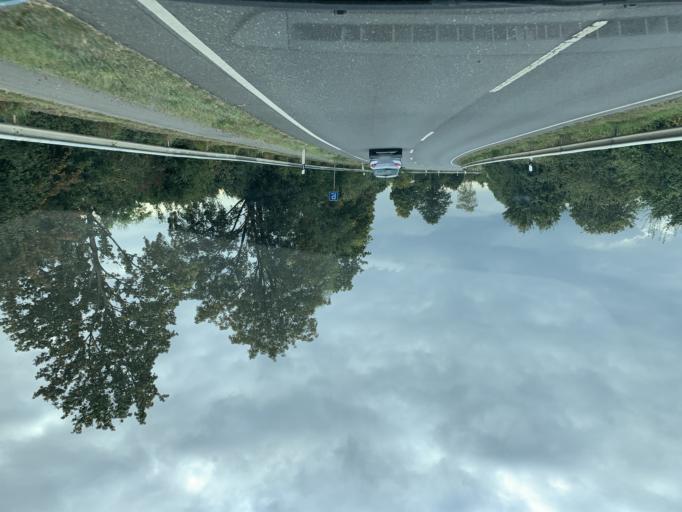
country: DE
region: North Rhine-Westphalia
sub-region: Regierungsbezirk Koln
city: Wassenberg
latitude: 51.0876
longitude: 6.1464
